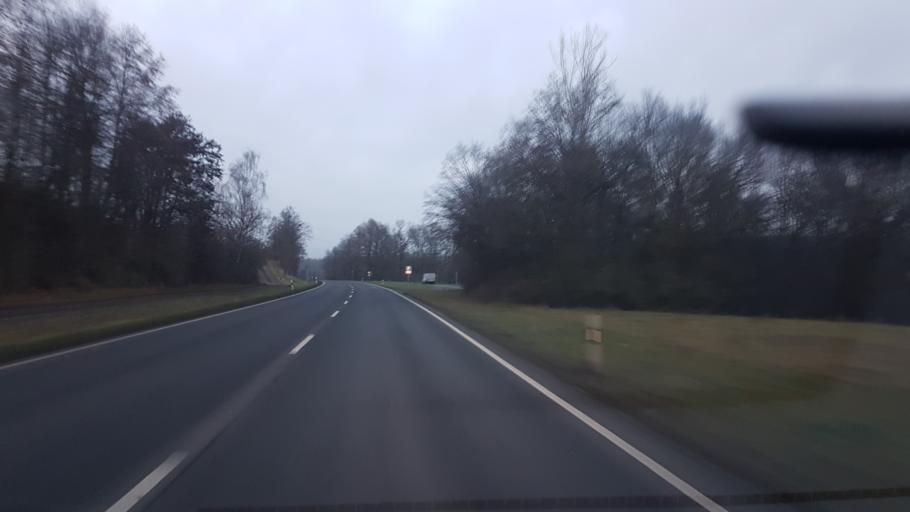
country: DE
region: Bavaria
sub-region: Regierungsbezirk Unterfranken
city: Rentweinsdorf
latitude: 50.0970
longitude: 10.7861
